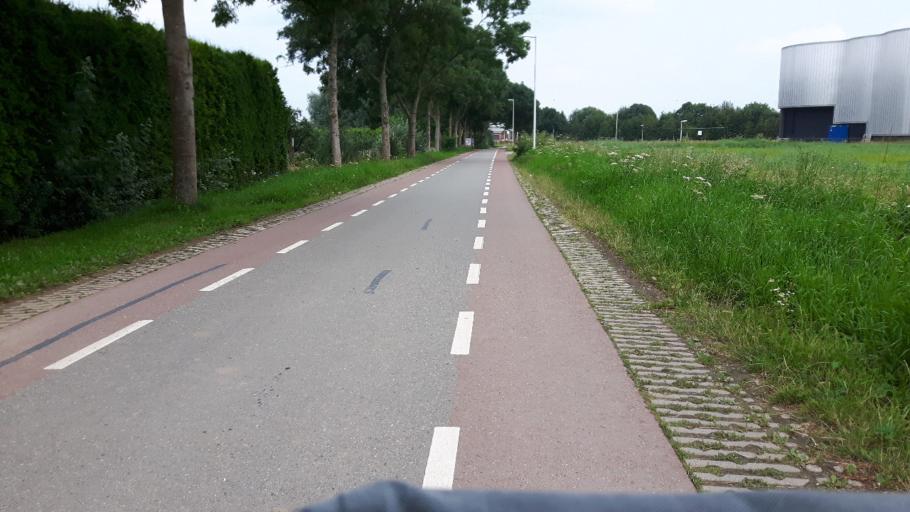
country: NL
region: Utrecht
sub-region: Gemeente Bunnik
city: Bunnik
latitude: 52.0595
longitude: 5.1898
